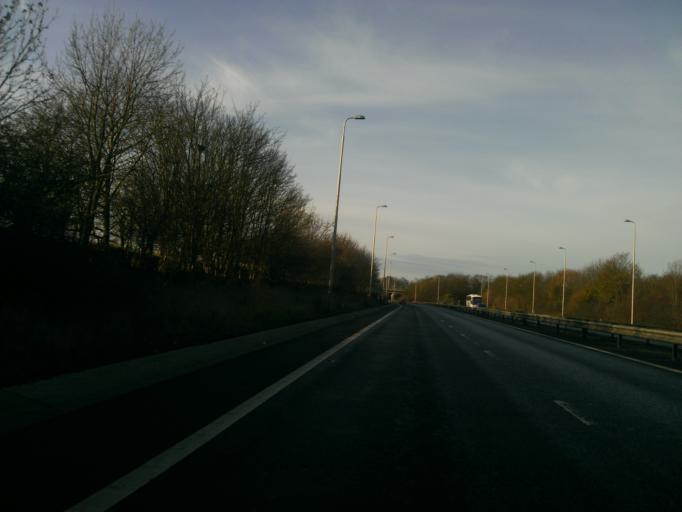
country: GB
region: England
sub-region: Essex
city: Witham
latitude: 51.7851
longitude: 0.6232
